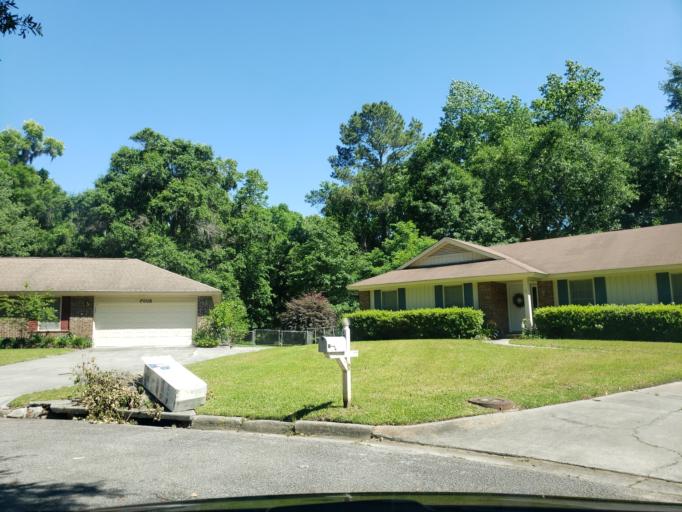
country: US
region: Georgia
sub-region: Chatham County
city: Isle of Hope
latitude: 31.9877
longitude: -81.0912
